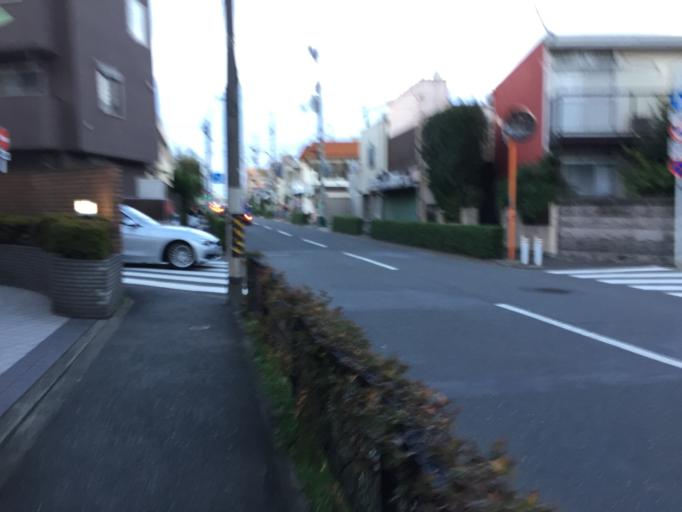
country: JP
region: Tokyo
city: Tokyo
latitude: 35.6389
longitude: 139.6434
